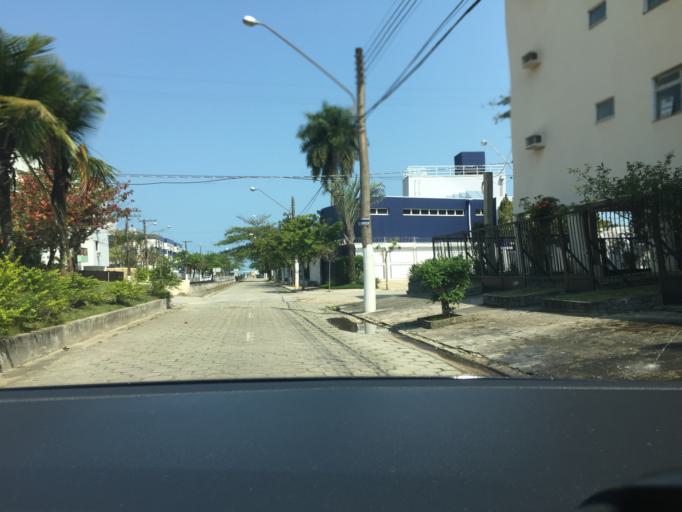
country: BR
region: Sao Paulo
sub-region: Guaruja
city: Guaruja
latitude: -23.9822
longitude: -46.2215
